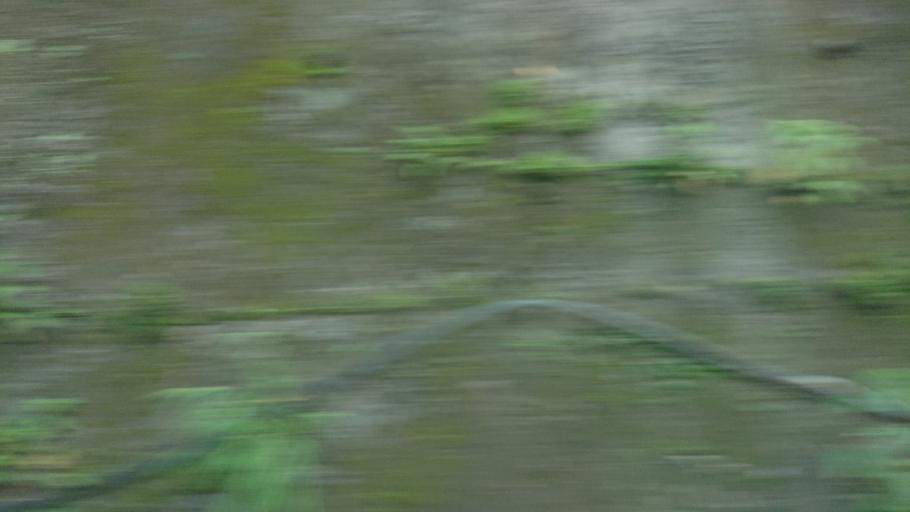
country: TW
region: Taiwan
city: Daxi
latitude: 24.8803
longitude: 121.3809
